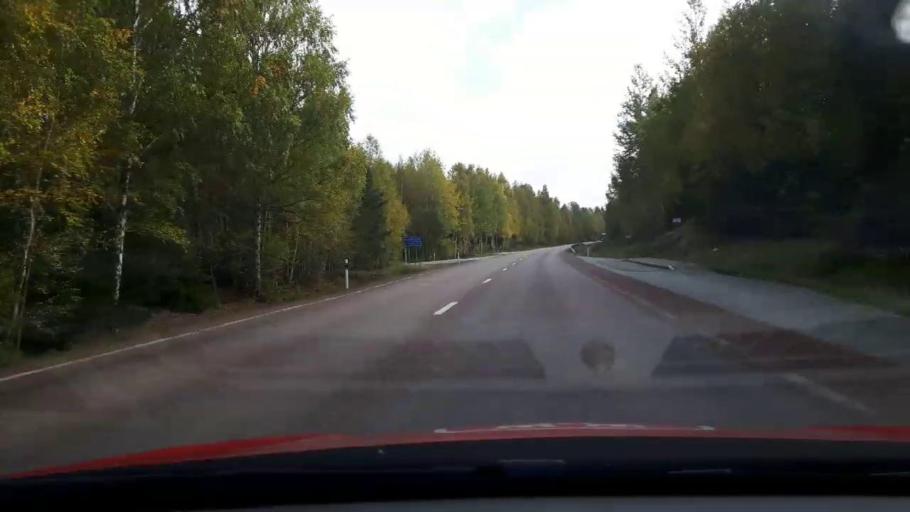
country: SE
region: Gaevleborg
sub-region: Ljusdals Kommun
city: Jaervsoe
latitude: 61.6442
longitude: 16.2185
